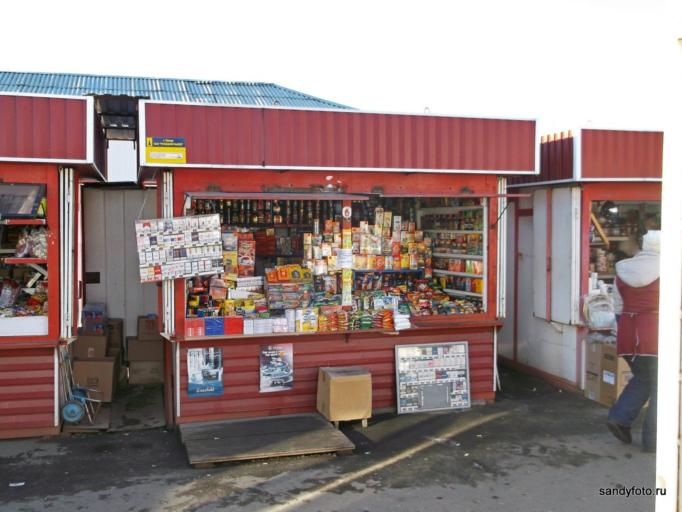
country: RU
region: Chelyabinsk
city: Troitsk
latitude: 54.0895
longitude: 61.5601
